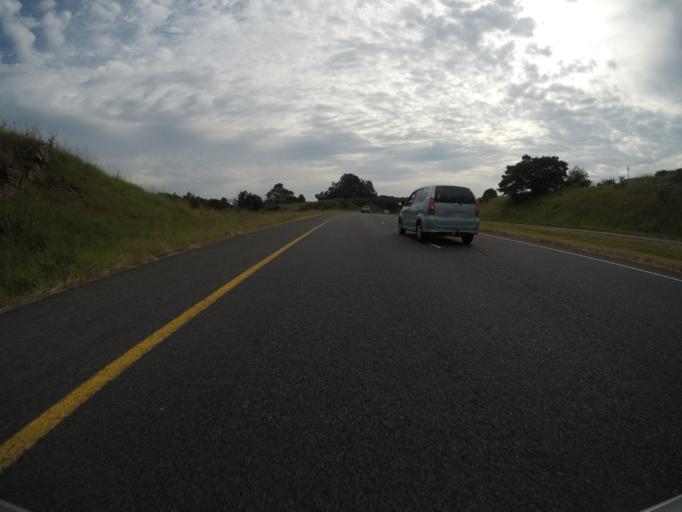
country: ZA
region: Eastern Cape
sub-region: Buffalo City Metropolitan Municipality
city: East London
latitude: -32.9687
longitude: 27.8734
